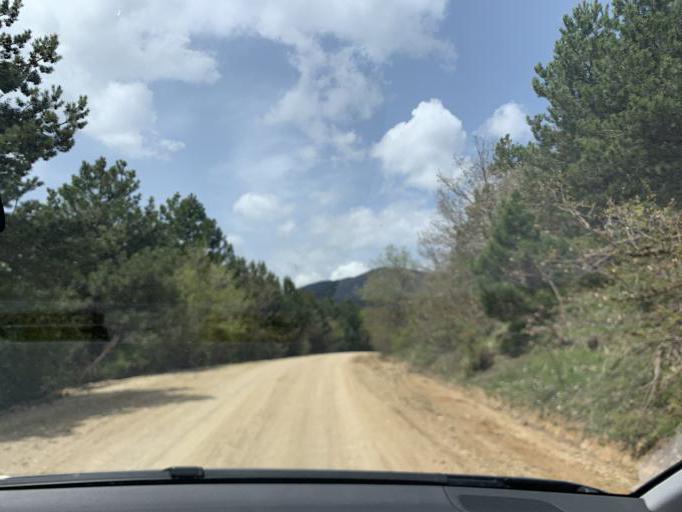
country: TR
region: Bolu
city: Bolu
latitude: 40.8304
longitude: 31.6754
